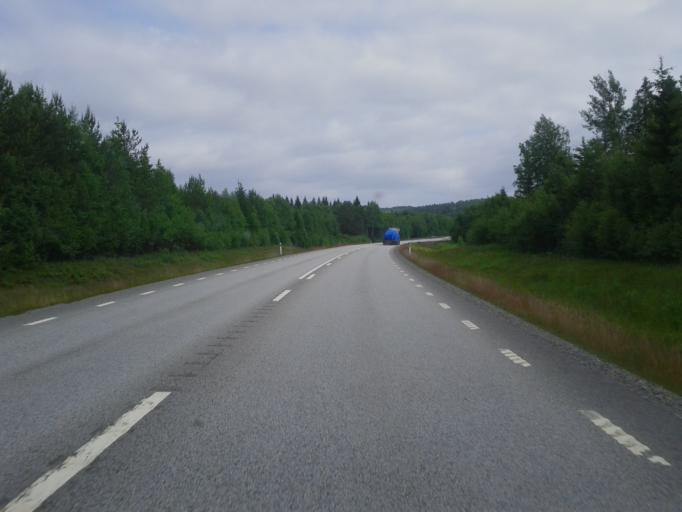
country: SE
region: Vaesterbotten
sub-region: Robertsfors Kommun
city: Robertsfors
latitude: 64.2909
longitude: 21.0777
